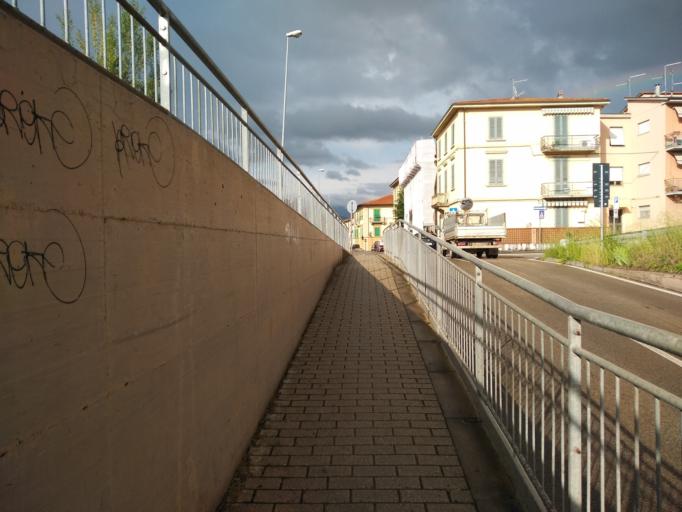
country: IT
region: Tuscany
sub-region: Province of Arezzo
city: San Giovanni Valdarno
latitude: 43.5621
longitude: 11.5316
